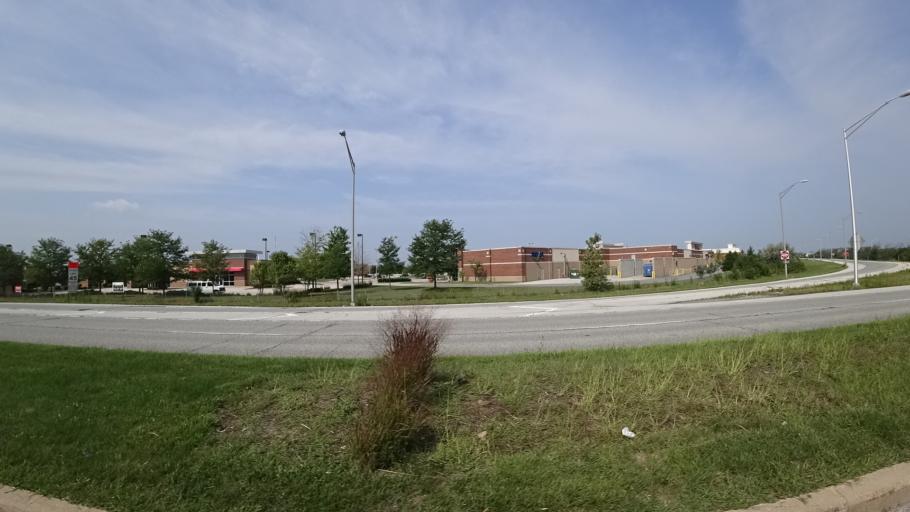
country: US
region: Illinois
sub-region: Cook County
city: Tinley Park
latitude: 41.5468
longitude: -87.7923
